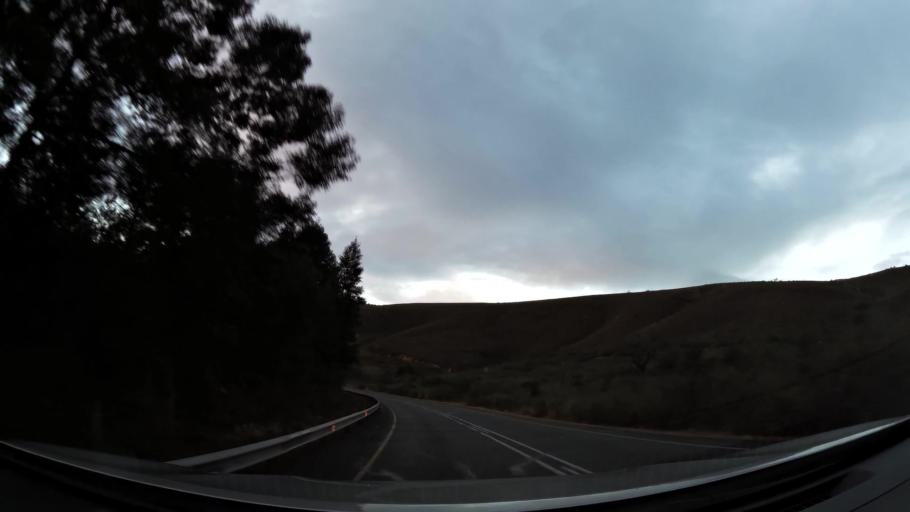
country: ZA
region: Western Cape
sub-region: Overberg District Municipality
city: Swellendam
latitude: -33.9894
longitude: 20.7147
